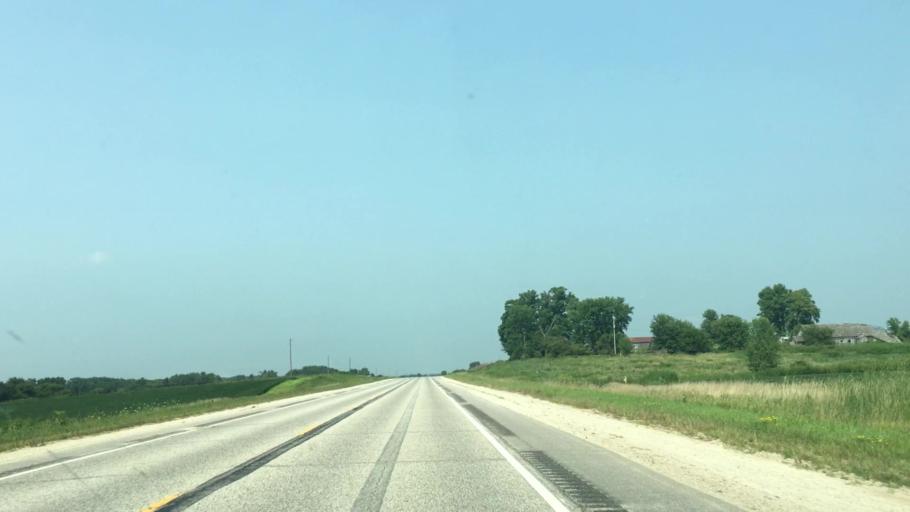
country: US
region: Iowa
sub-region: Fayette County
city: Fayette
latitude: 42.7941
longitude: -91.8050
